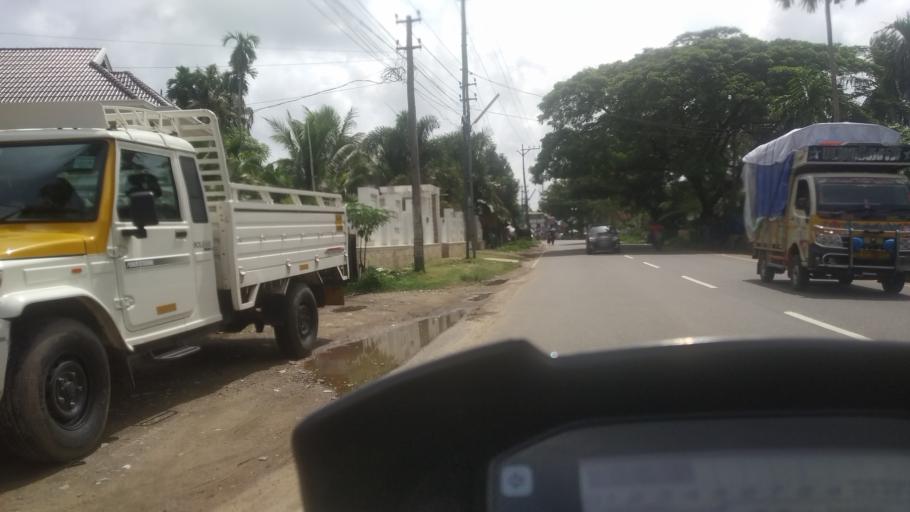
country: IN
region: Kerala
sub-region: Ernakulam
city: Aluva
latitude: 10.1287
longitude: 76.3035
